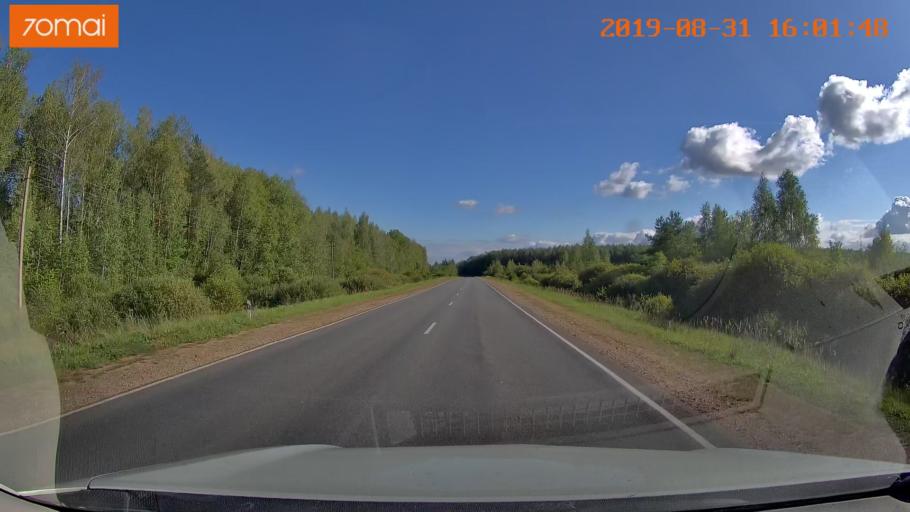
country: RU
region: Kaluga
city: Yukhnov
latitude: 54.6842
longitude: 35.2936
